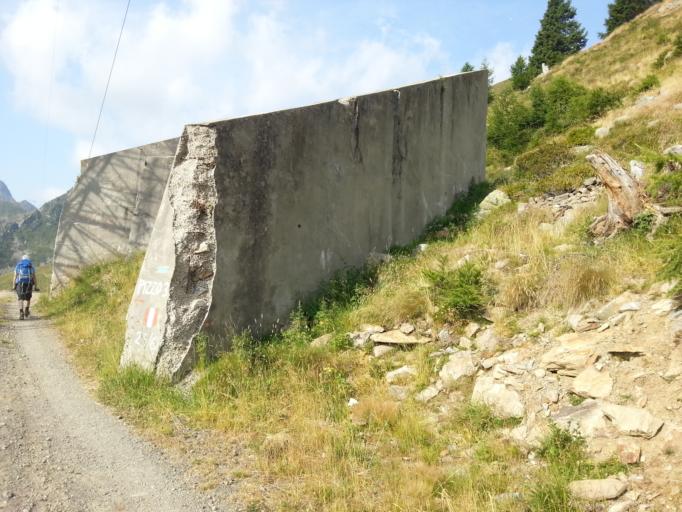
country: IT
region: Lombardy
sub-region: Provincia di Sondrio
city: Gerola Alta
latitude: 46.0480
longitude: 9.5316
